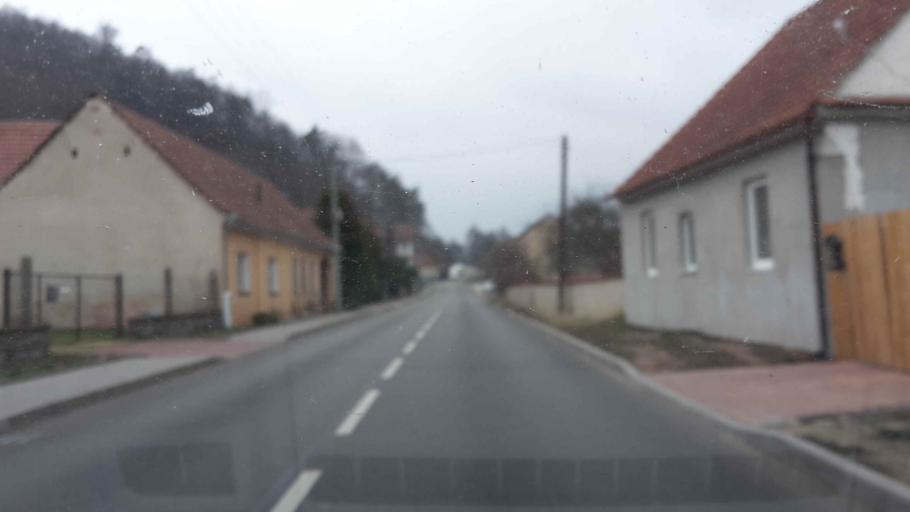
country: CZ
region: South Moravian
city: Predklasteri
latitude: 49.3742
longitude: 16.3864
